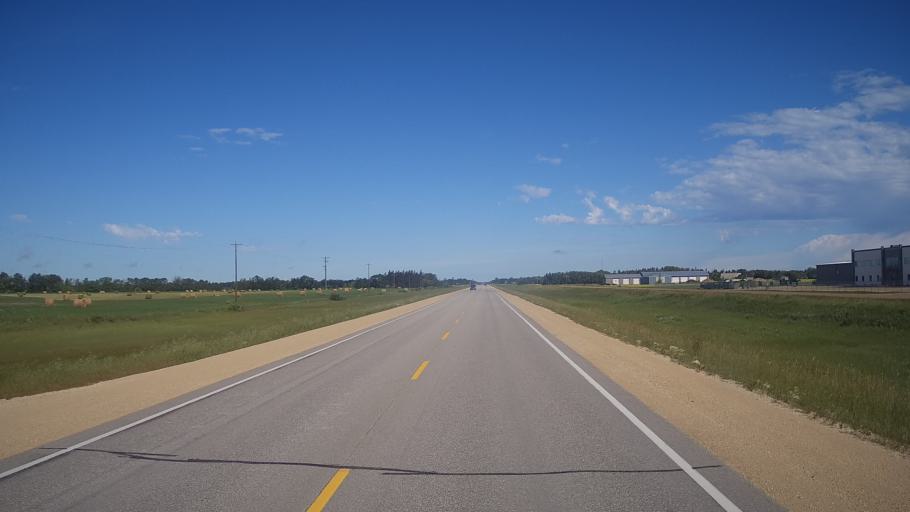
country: CA
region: Manitoba
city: Stonewall
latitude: 50.1970
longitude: -97.6466
